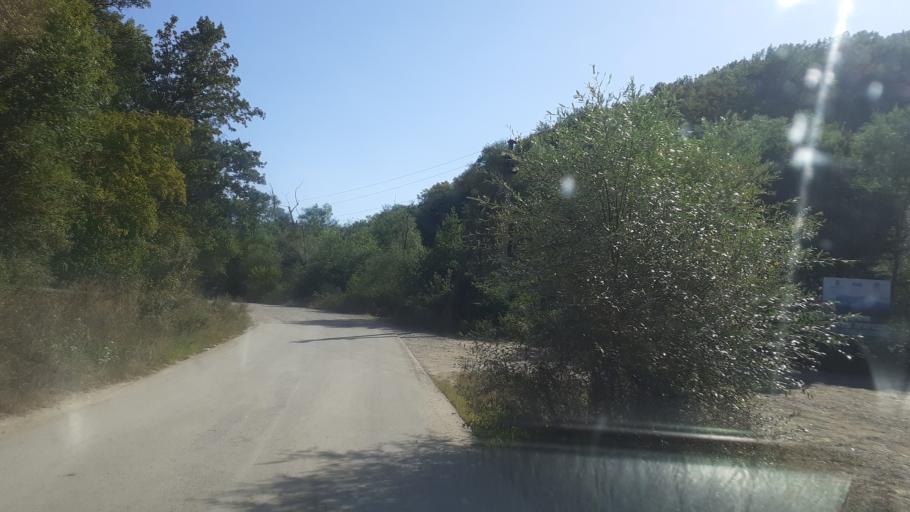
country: RU
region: Krasnodarskiy
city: Azovskaya
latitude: 44.7270
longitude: 38.5345
